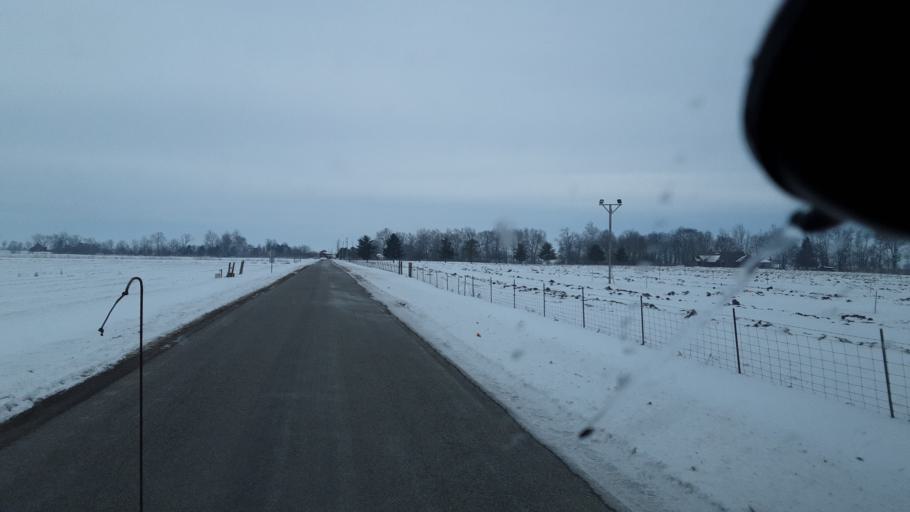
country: US
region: Ohio
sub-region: Union County
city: Marysville
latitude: 40.1227
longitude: -83.4237
